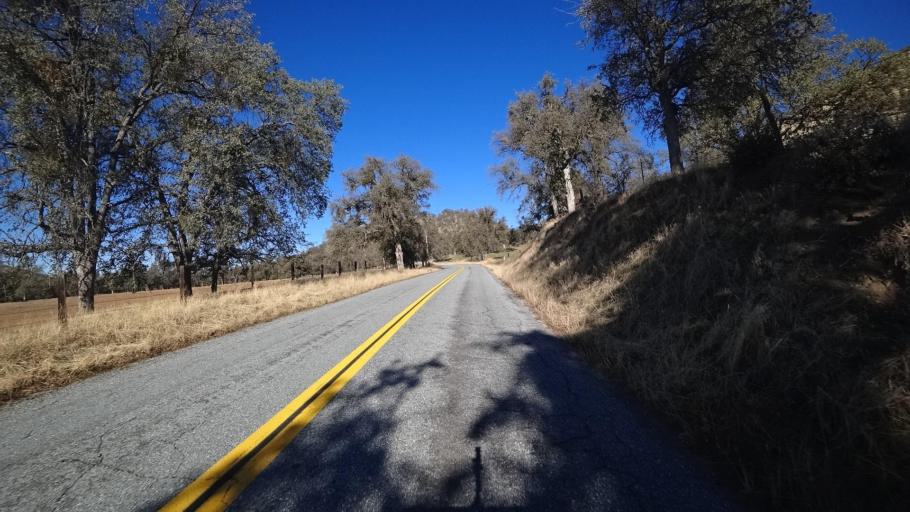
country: US
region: California
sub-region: Kern County
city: Alta Sierra
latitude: 35.7959
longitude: -118.7109
